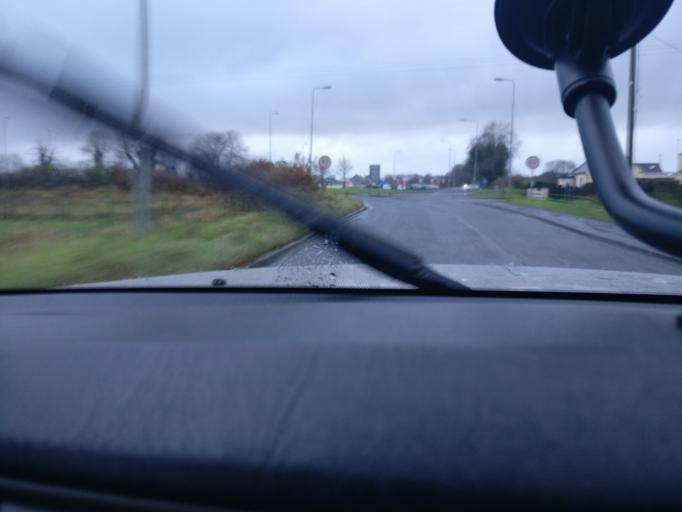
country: IE
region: Leinster
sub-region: An Iarmhi
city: Kinnegad
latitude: 53.4530
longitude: -7.1224
